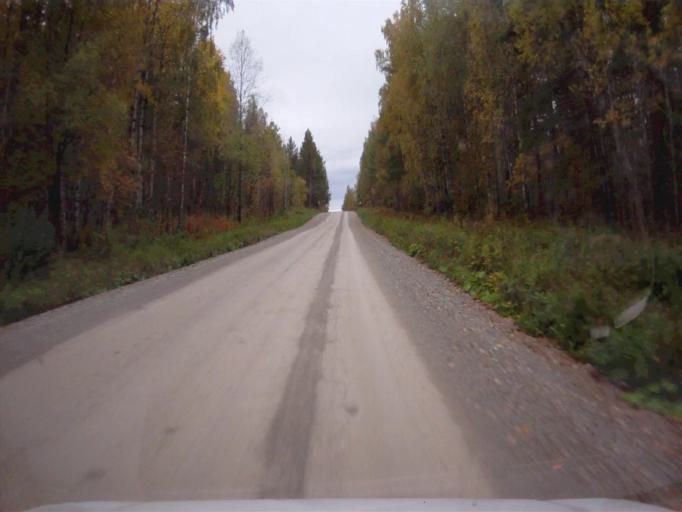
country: RU
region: Chelyabinsk
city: Nyazepetrovsk
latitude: 56.0693
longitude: 59.4321
